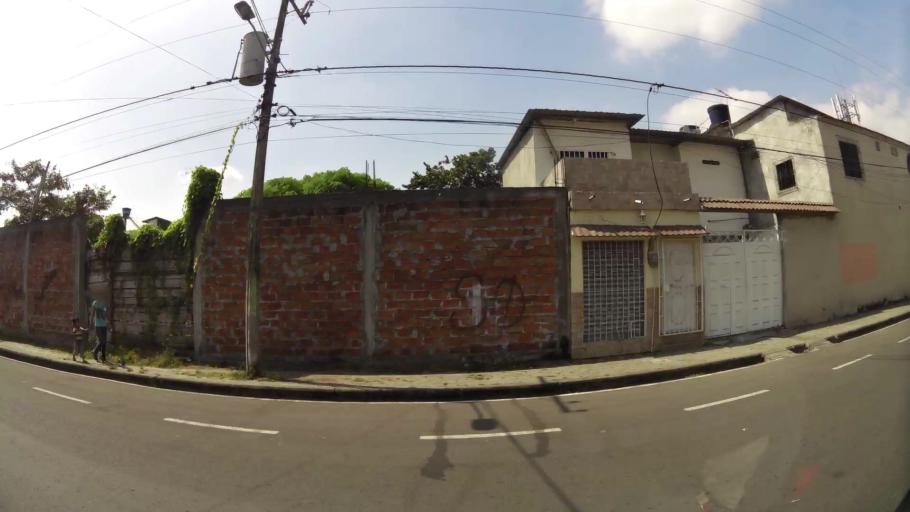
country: EC
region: Guayas
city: Eloy Alfaro
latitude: -2.1552
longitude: -79.8403
